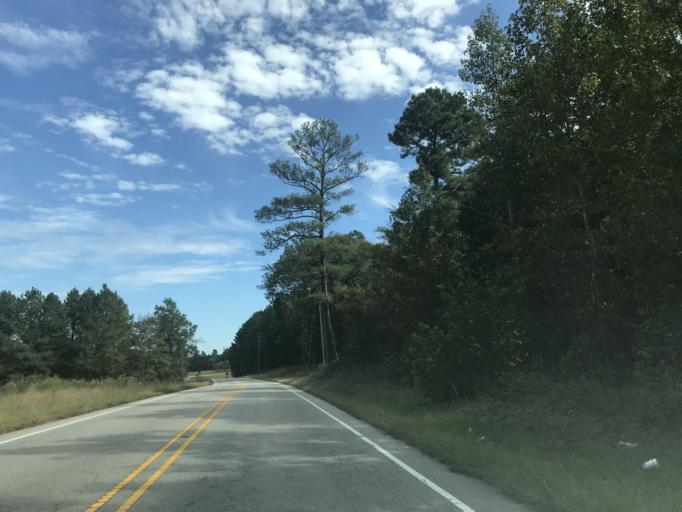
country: US
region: North Carolina
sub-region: Wake County
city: Rolesville
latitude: 35.8791
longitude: -78.4799
